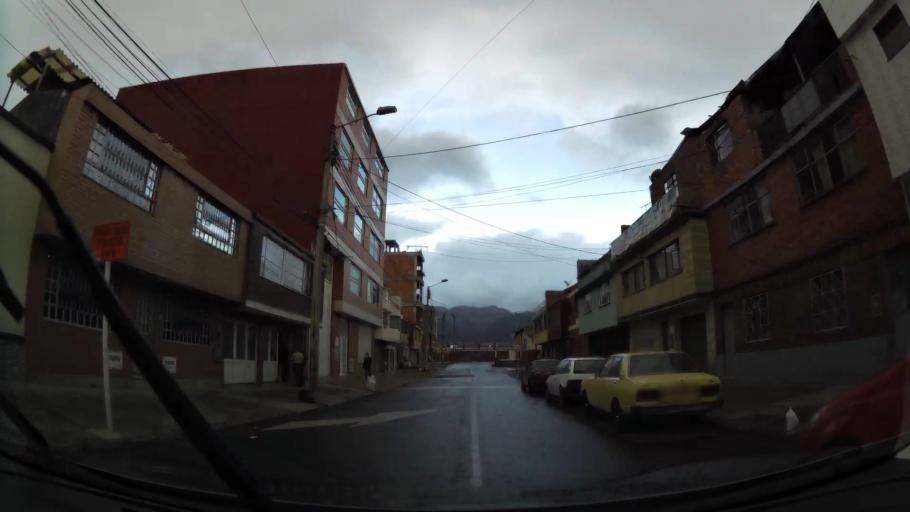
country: CO
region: Bogota D.C.
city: Barrio San Luis
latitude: 4.6733
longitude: -74.0781
